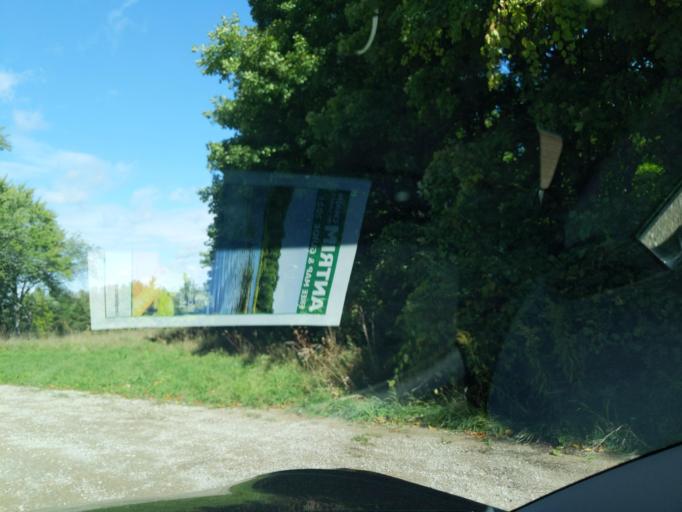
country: US
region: Michigan
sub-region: Antrim County
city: Elk Rapids
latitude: 44.9448
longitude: -85.3326
